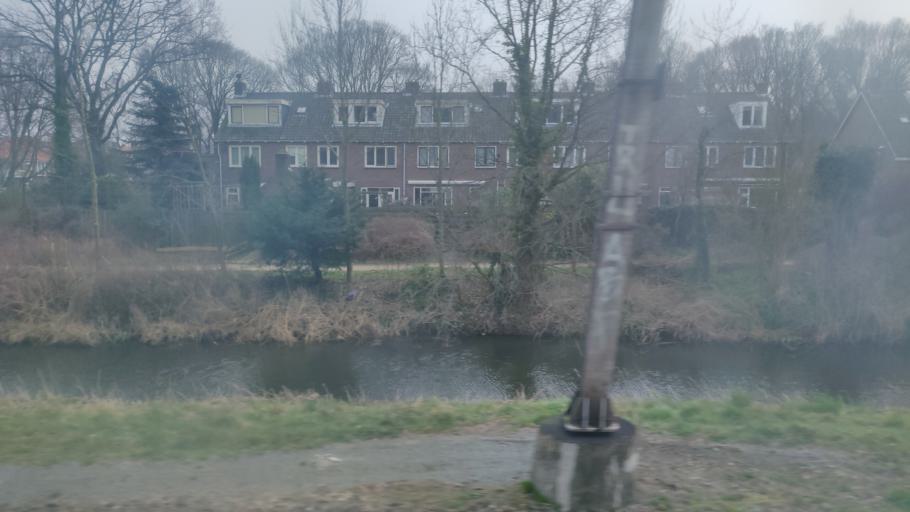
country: NL
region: North Holland
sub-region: Gemeente Alkmaar
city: Alkmaar
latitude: 52.6316
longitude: 4.7300
